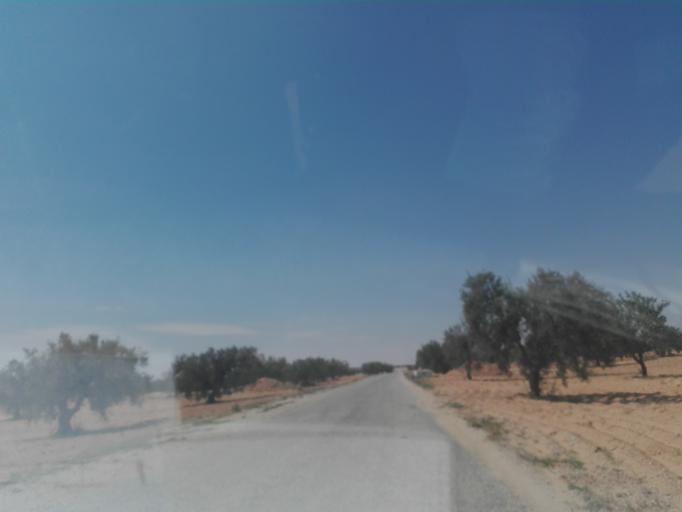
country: TN
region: Safaqis
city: Bi'r `Ali Bin Khalifah
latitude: 34.6258
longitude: 10.3708
